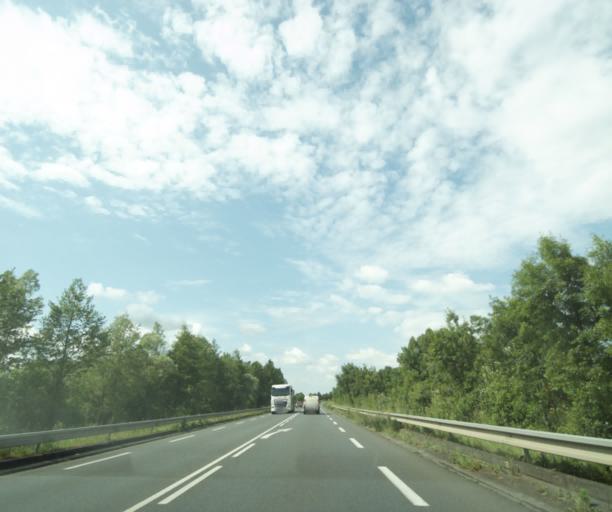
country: FR
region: Pays de la Loire
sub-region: Departement de Maine-et-Loire
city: Distre
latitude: 47.2174
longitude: -0.1163
